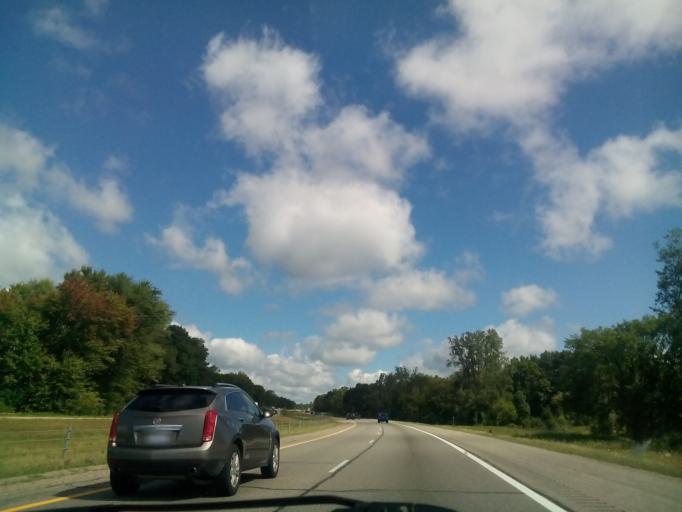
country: US
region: Michigan
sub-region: Livingston County
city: Brighton
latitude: 42.5618
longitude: -83.7402
